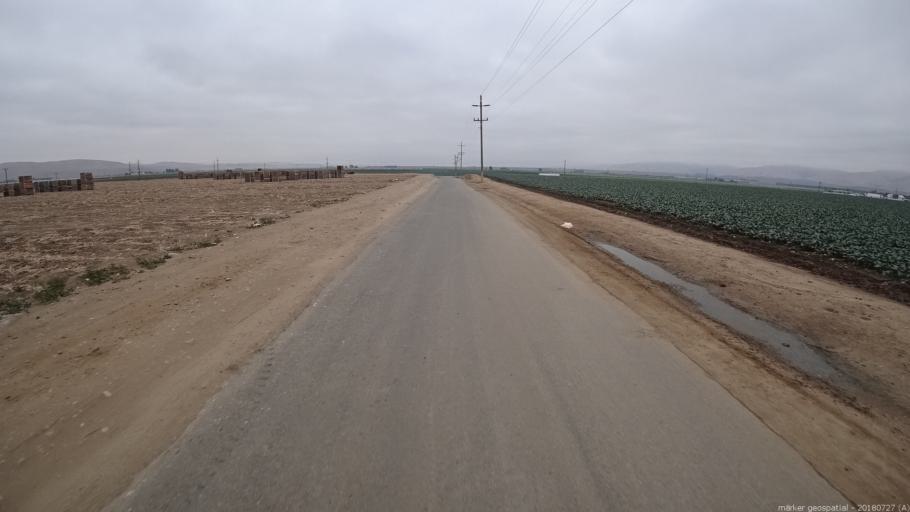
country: US
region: California
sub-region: Monterey County
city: Greenfield
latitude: 36.3290
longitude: -121.2259
